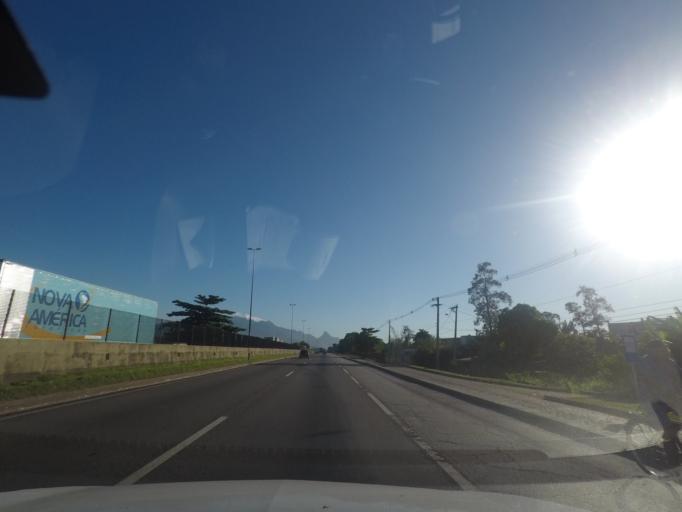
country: BR
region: Rio de Janeiro
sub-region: Duque De Caxias
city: Duque de Caxias
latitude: -22.6628
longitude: -43.2561
